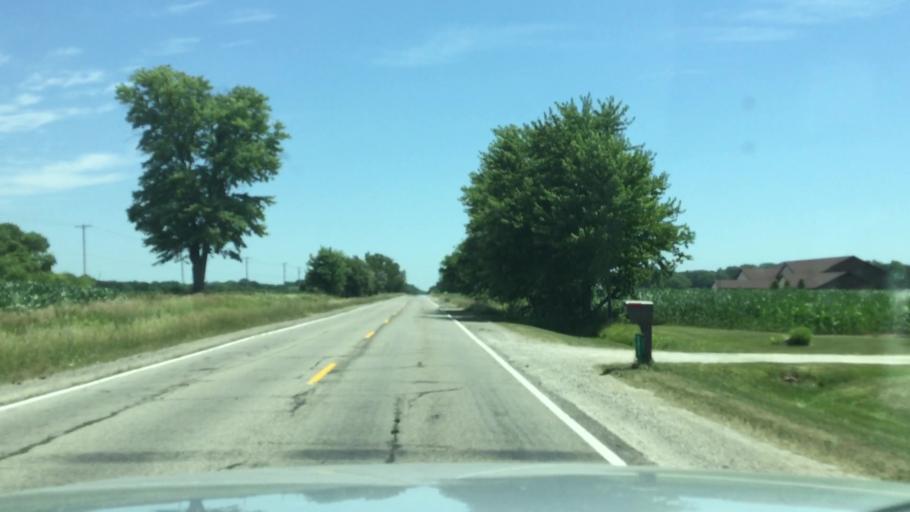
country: US
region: Michigan
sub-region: Genesee County
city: Swartz Creek
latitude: 42.9430
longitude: -83.7887
